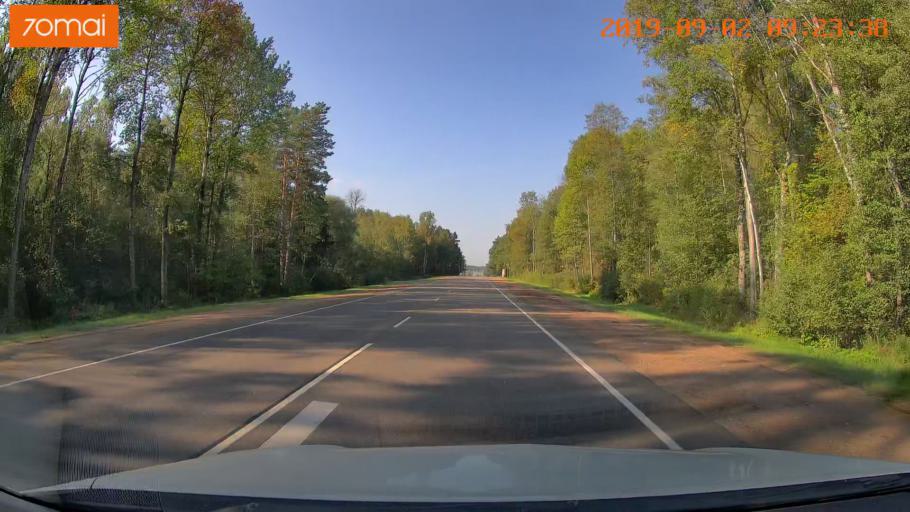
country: RU
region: Kaluga
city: Yukhnov
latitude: 54.7739
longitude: 35.3104
